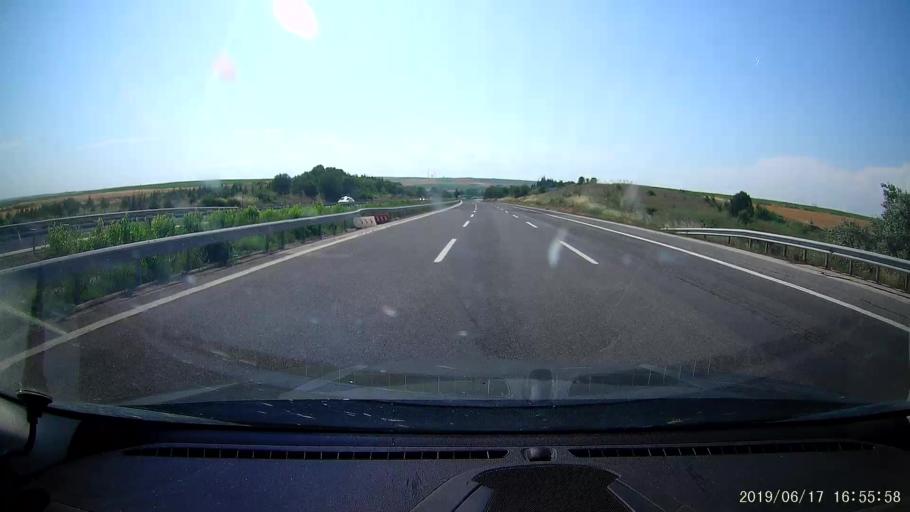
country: TR
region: Edirne
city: Haskoy
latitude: 41.5830
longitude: 26.9506
